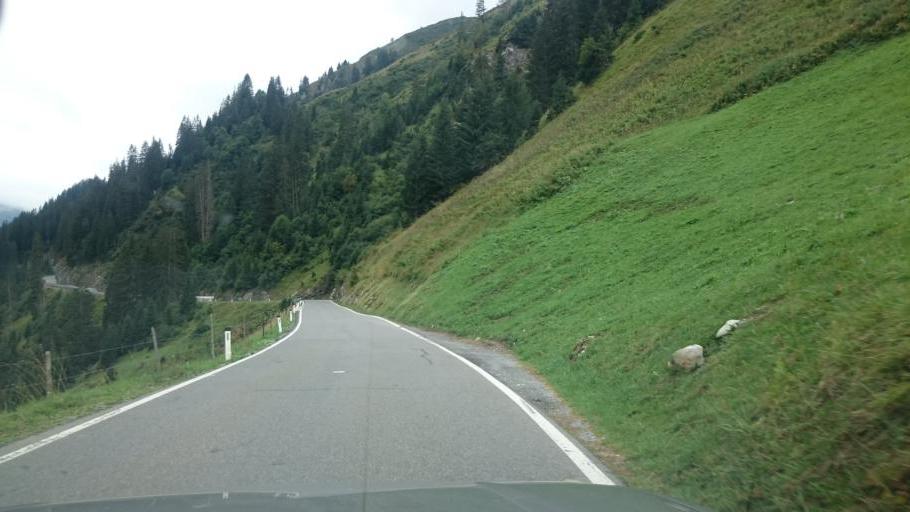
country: AT
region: Vorarlberg
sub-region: Politischer Bezirk Bregenz
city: Warth
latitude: 47.2502
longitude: 10.1784
